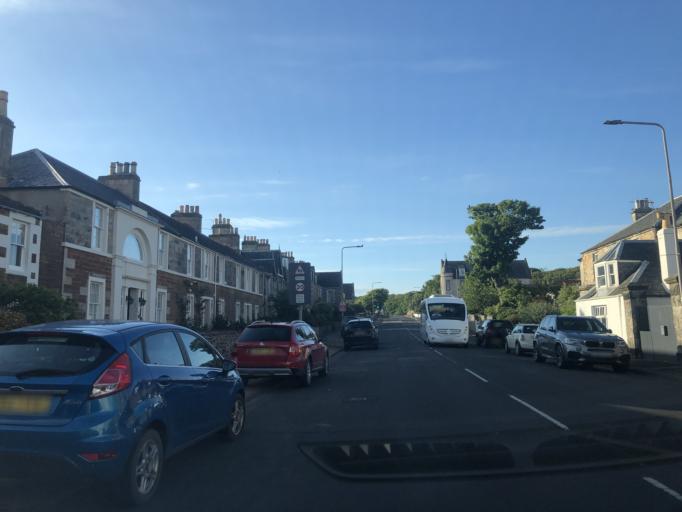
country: GB
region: Scotland
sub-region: Fife
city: Saint Monance
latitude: 56.1913
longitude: -2.8217
